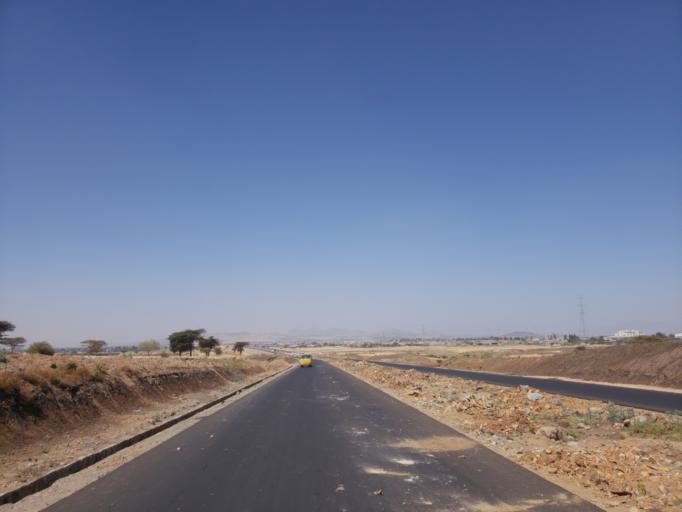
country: ET
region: Oromiya
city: Mojo
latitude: 8.5662
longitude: 39.1520
